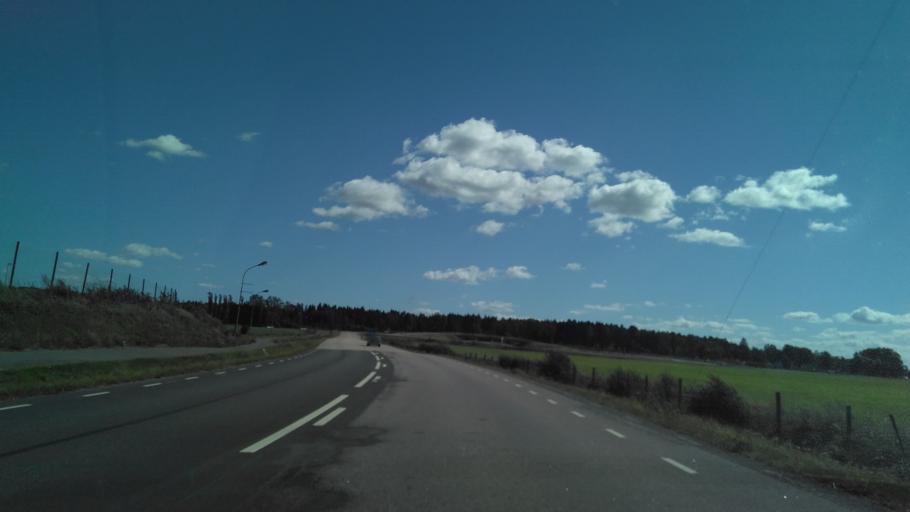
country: SE
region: Vaestra Goetaland
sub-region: Skara Kommun
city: Axvall
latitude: 58.4000
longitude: 13.5538
